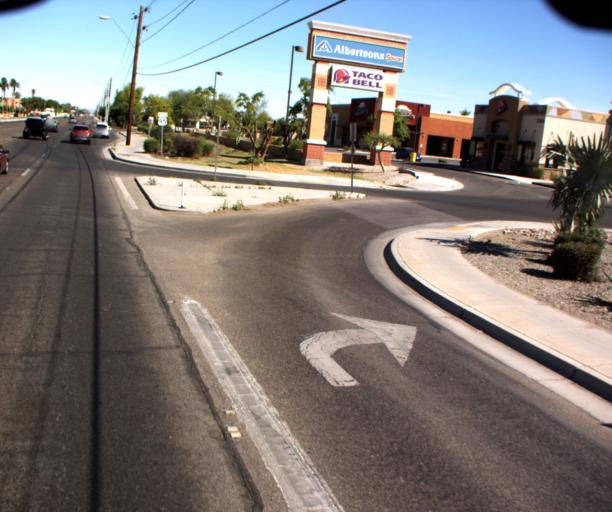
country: US
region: Arizona
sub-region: Yuma County
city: Yuma
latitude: 32.6845
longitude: -114.6503
